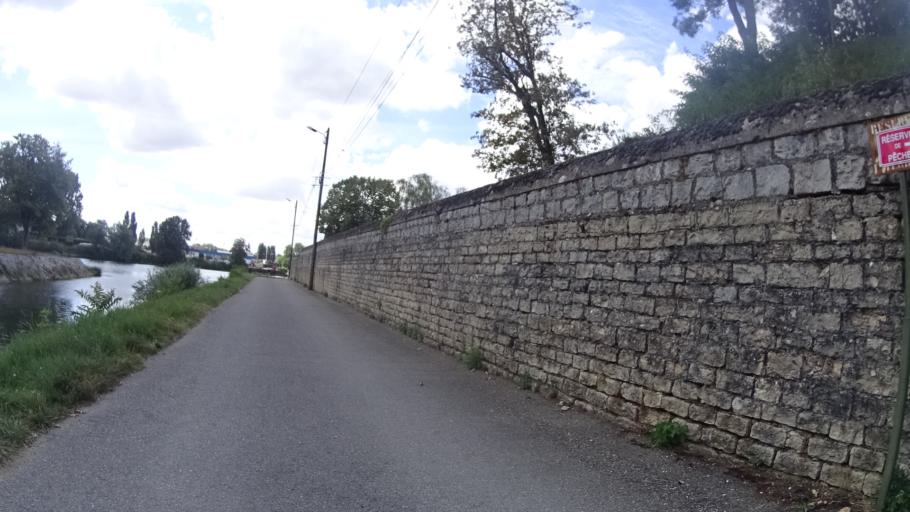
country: FR
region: Franche-Comte
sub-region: Departement du Jura
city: Dole
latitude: 47.0884
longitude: 5.4918
